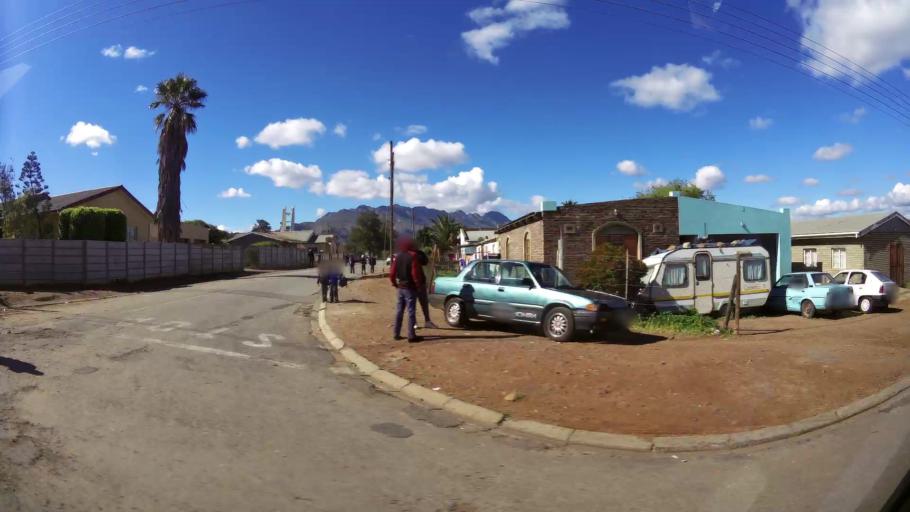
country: ZA
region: Western Cape
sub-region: Cape Winelands District Municipality
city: Ashton
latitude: -33.8329
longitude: 20.0433
